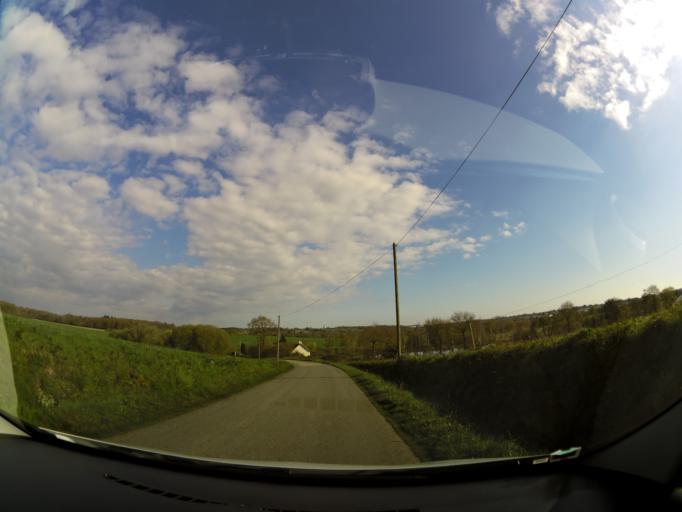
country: FR
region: Brittany
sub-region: Departement d'Ille-et-Vilaine
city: Laille
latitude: 47.9513
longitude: -1.6984
